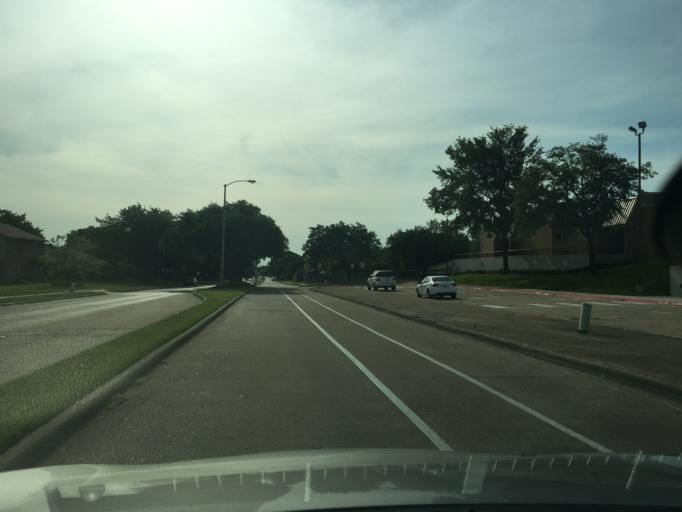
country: US
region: Texas
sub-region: Dallas County
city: Richardson
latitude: 32.9678
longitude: -96.6902
